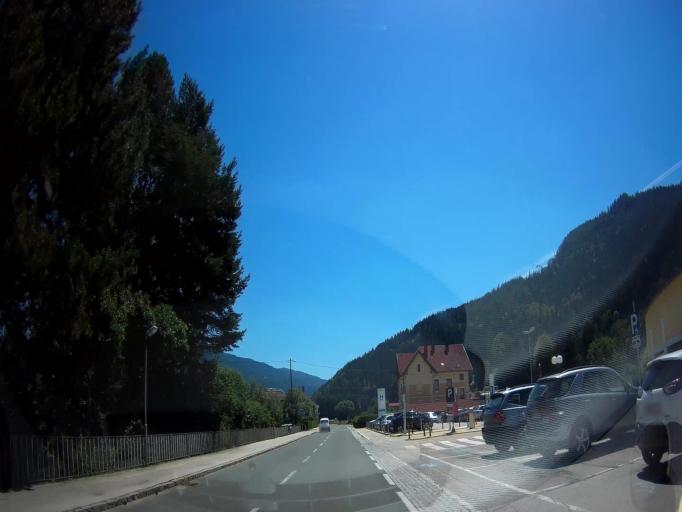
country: AT
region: Carinthia
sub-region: Politischer Bezirk Sankt Veit an der Glan
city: Friesach
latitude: 46.9474
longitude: 14.4116
